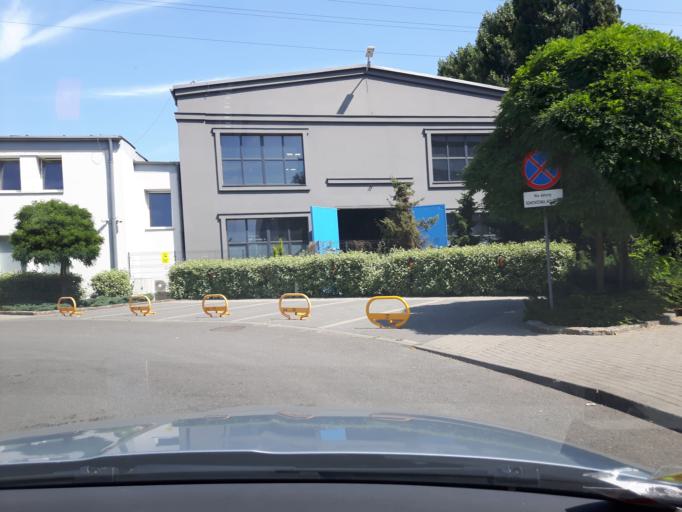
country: PL
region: Pomeranian Voivodeship
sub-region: Gdansk
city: Gdansk
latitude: 54.3713
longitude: 18.6537
